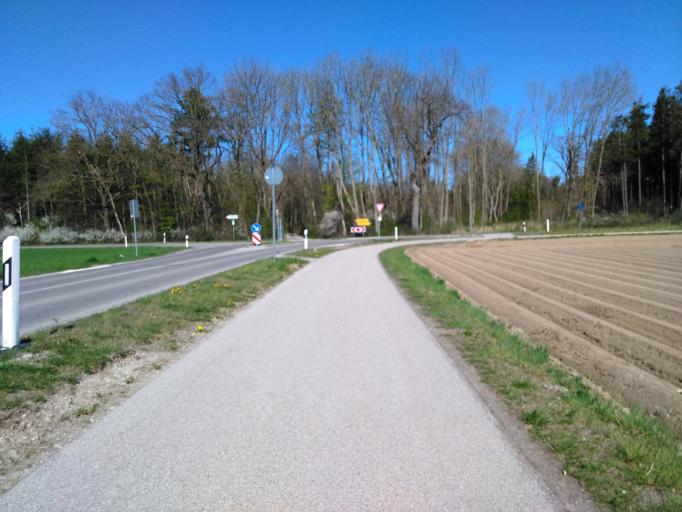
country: DE
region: Bavaria
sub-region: Upper Bavaria
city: Mammendorf
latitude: 48.2116
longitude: 11.1904
